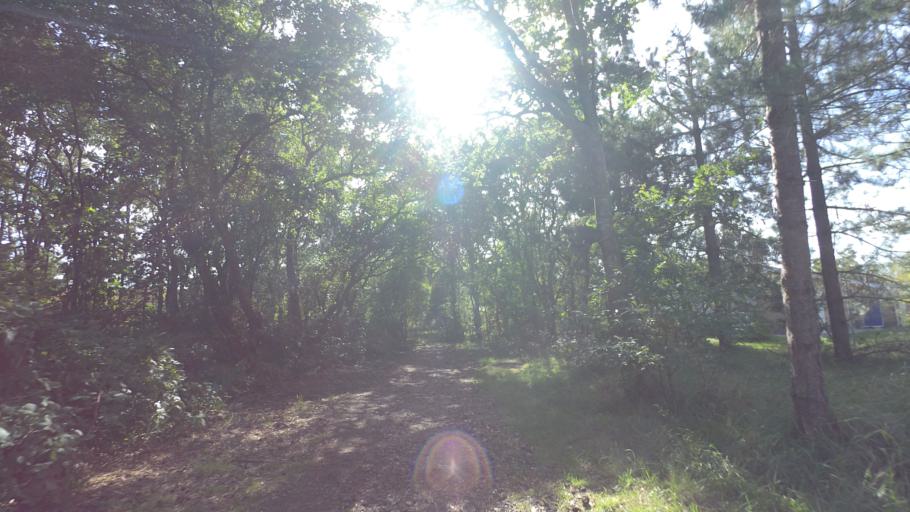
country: NL
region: Friesland
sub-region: Gemeente Ameland
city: Hollum
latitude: 53.4498
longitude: 5.6956
